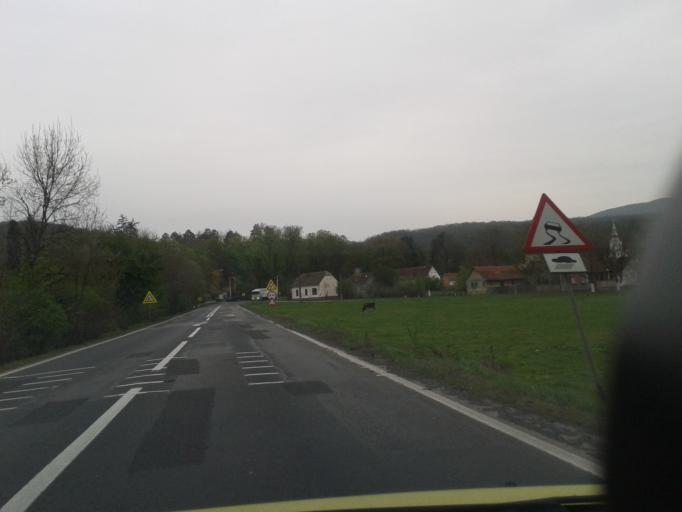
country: RO
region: Arad
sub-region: Comuna Ususau
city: Ususau
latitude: 46.1058
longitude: 21.8148
